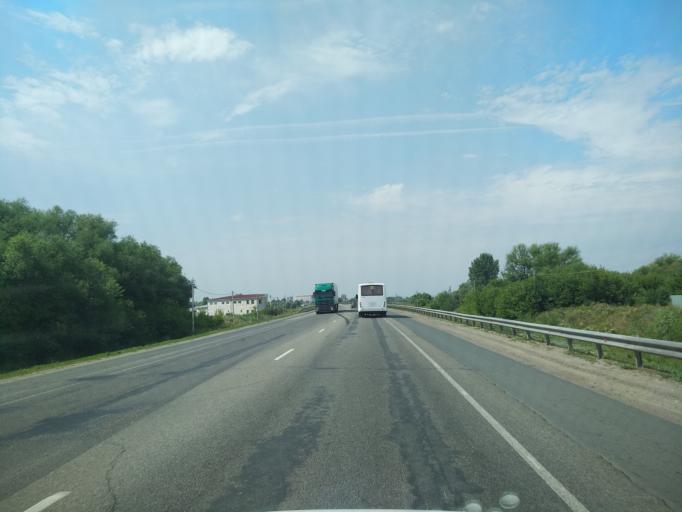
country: RU
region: Voronezj
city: Somovo
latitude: 51.6881
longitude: 39.3573
